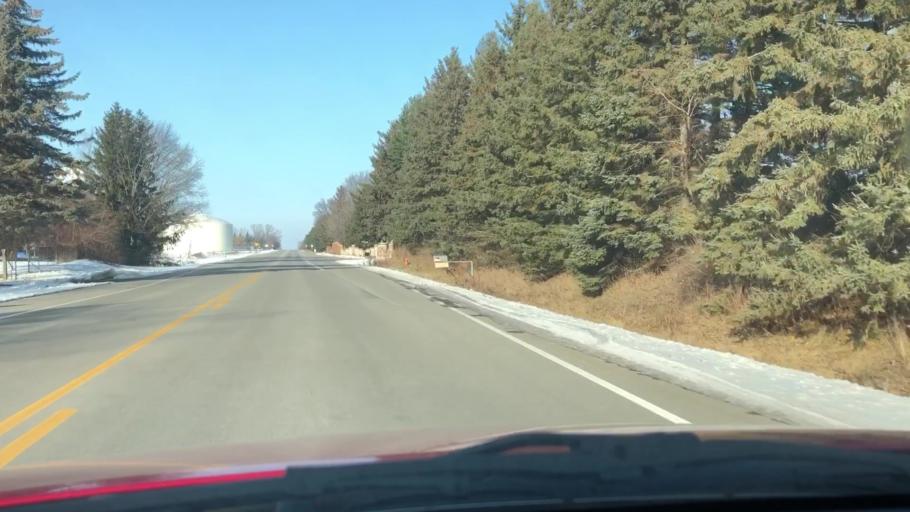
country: US
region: Wisconsin
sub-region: Outagamie County
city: Kimberly
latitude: 44.3320
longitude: -88.3750
